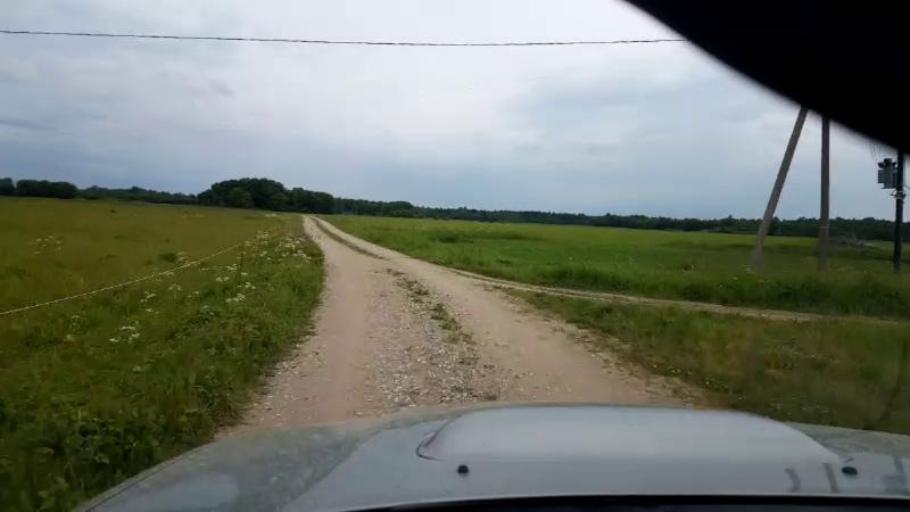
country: EE
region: Paernumaa
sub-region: Tootsi vald
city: Tootsi
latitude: 58.5910
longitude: 24.6597
